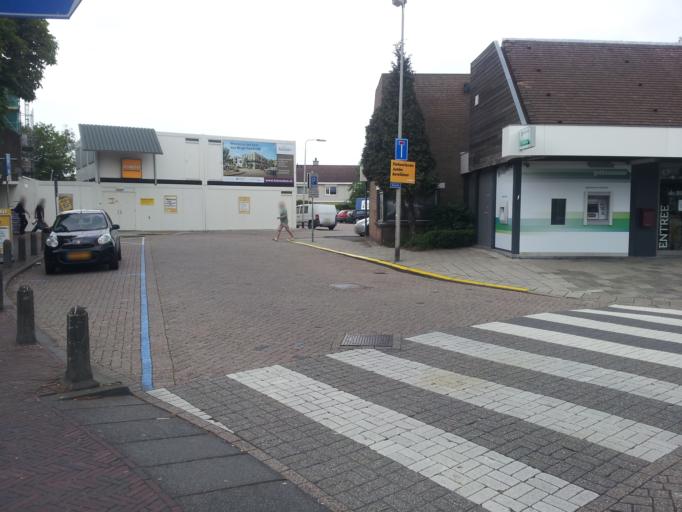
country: NL
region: South Holland
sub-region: Gemeente Lansingerland
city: Bergschenhoek
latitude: 51.9894
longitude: 4.5017
